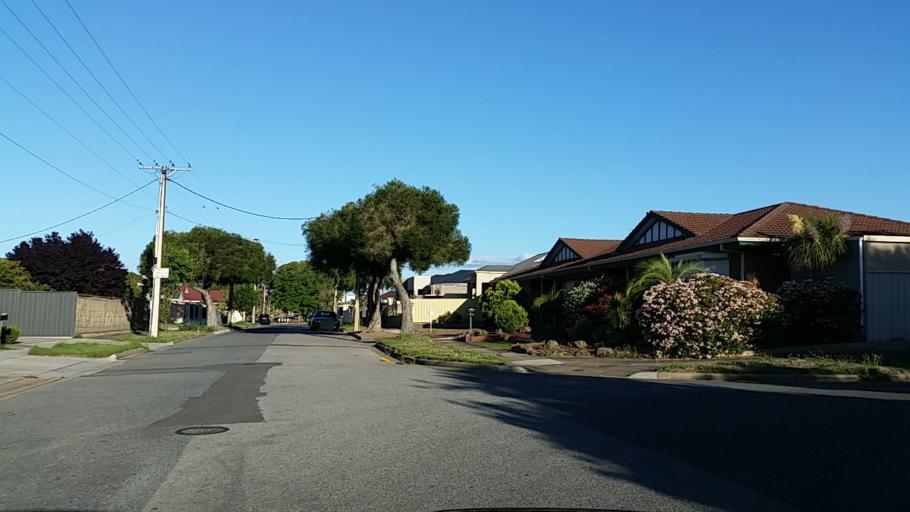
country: AU
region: South Australia
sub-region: Charles Sturt
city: Royal Park
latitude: -34.8780
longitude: 138.5051
